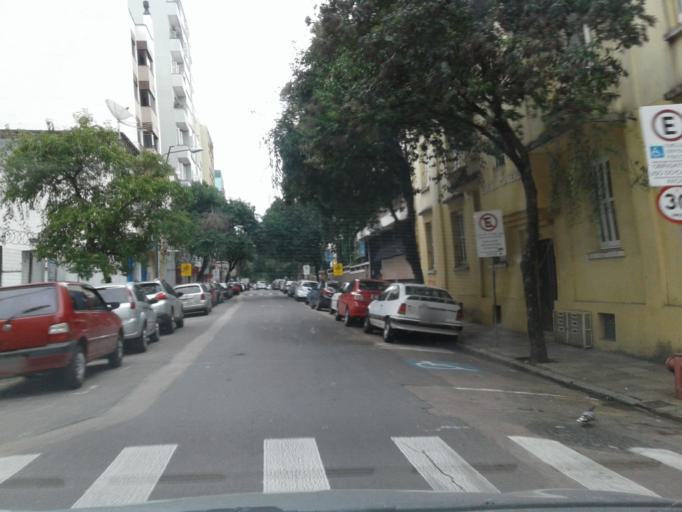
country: BR
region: Rio Grande do Sul
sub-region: Porto Alegre
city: Porto Alegre
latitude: -30.0323
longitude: -51.2330
